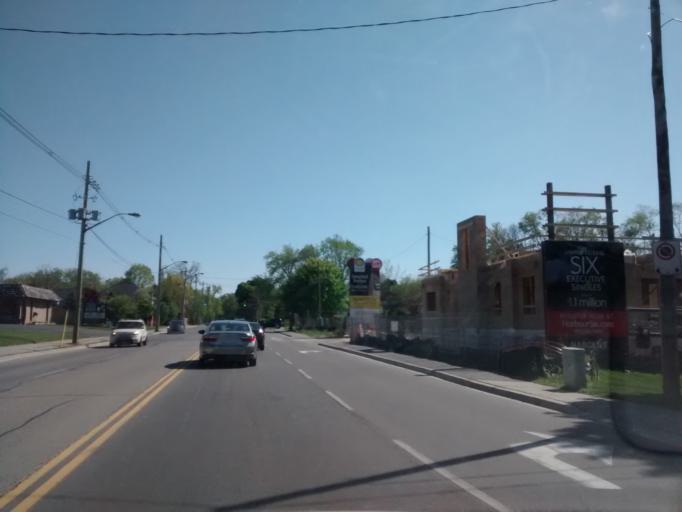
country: CA
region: Ontario
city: Oakville
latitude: 43.3908
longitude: -79.7149
